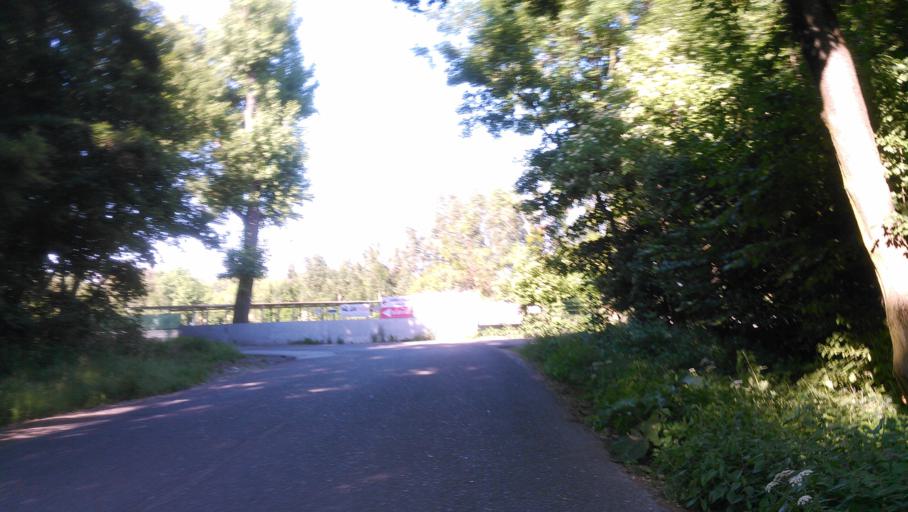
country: SK
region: Bratislavsky
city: Bratislava
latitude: 48.1243
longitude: 17.1358
